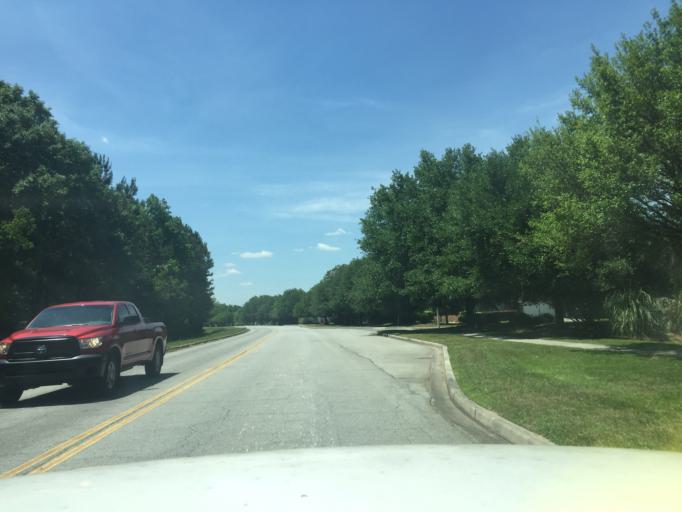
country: US
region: Georgia
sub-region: Chatham County
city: Georgetown
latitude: 32.0025
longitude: -81.2627
